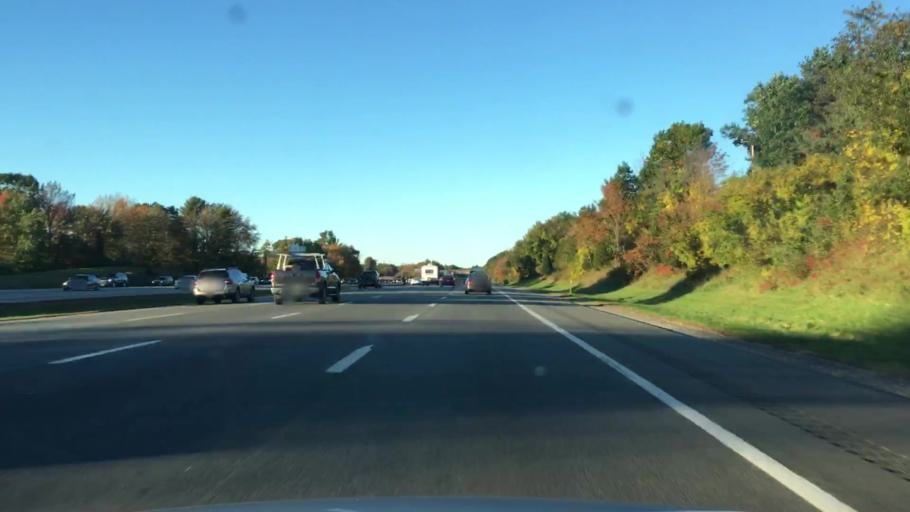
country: US
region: New Hampshire
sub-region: Rockingham County
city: North Hampton
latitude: 42.9751
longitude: -70.8535
